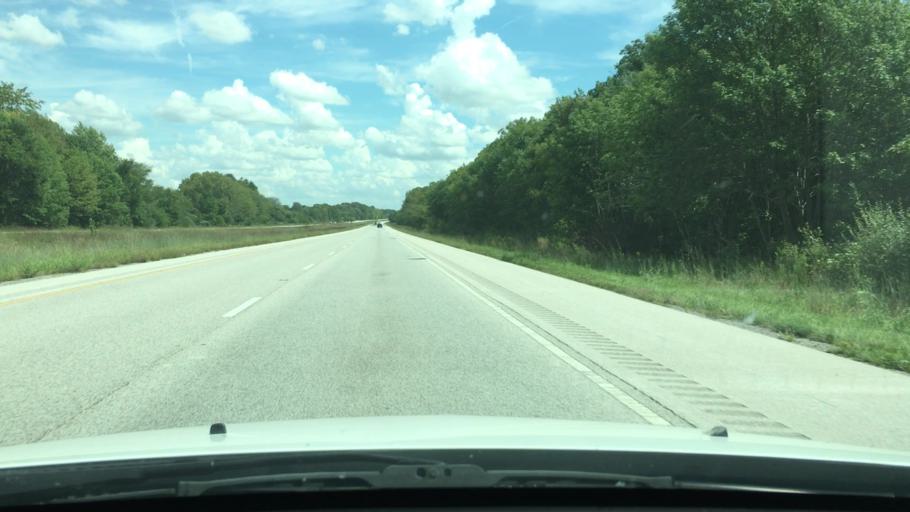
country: US
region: Illinois
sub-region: Scott County
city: Winchester
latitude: 39.6812
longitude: -90.4103
